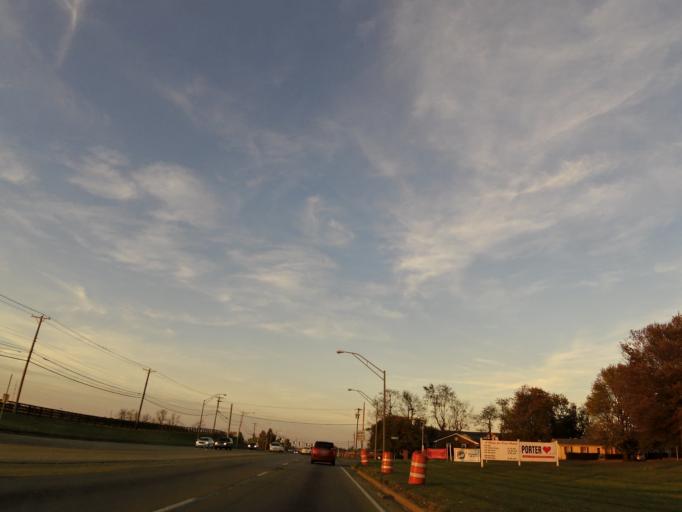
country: US
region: Kentucky
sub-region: Fayette County
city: Monticello
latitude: 37.9734
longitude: -84.5310
